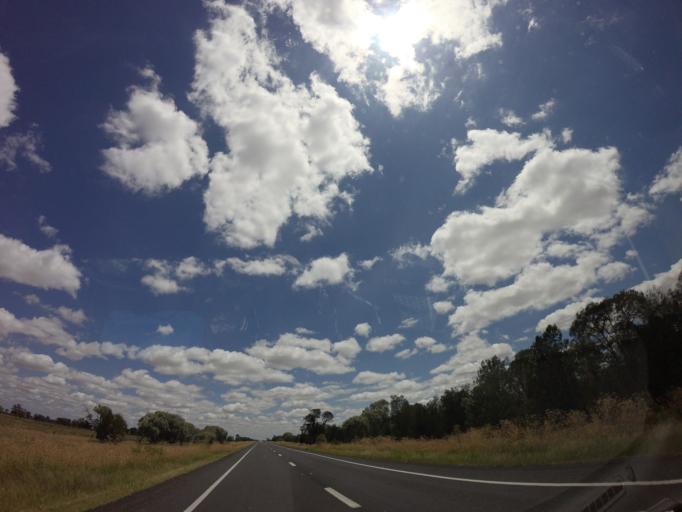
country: AU
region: New South Wales
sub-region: Moree Plains
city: Moree
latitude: -29.0685
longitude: 150.0438
